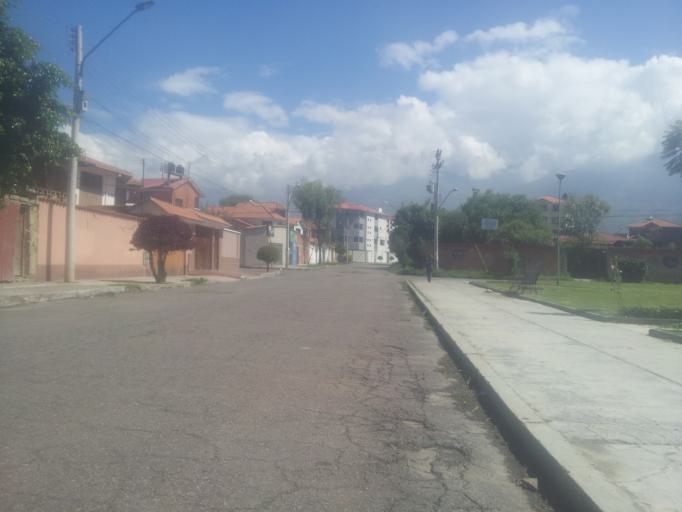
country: BO
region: Cochabamba
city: Cochabamba
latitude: -17.3696
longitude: -66.1775
